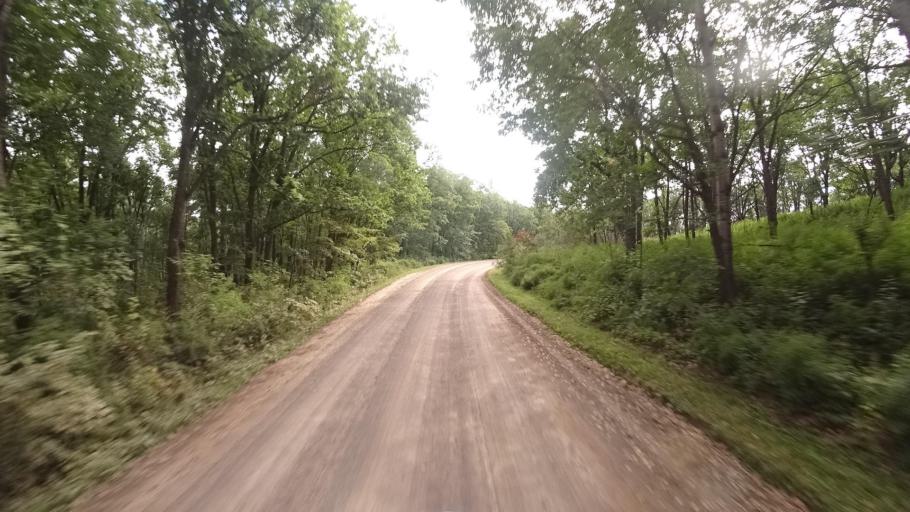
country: RU
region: Primorskiy
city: Dostoyevka
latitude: 44.3529
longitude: 133.5208
